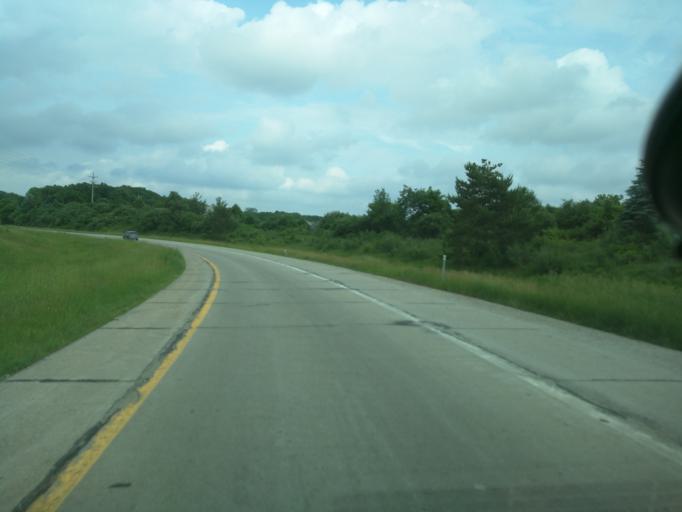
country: US
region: Michigan
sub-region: Clinton County
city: DeWitt
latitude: 42.8053
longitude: -84.6016
